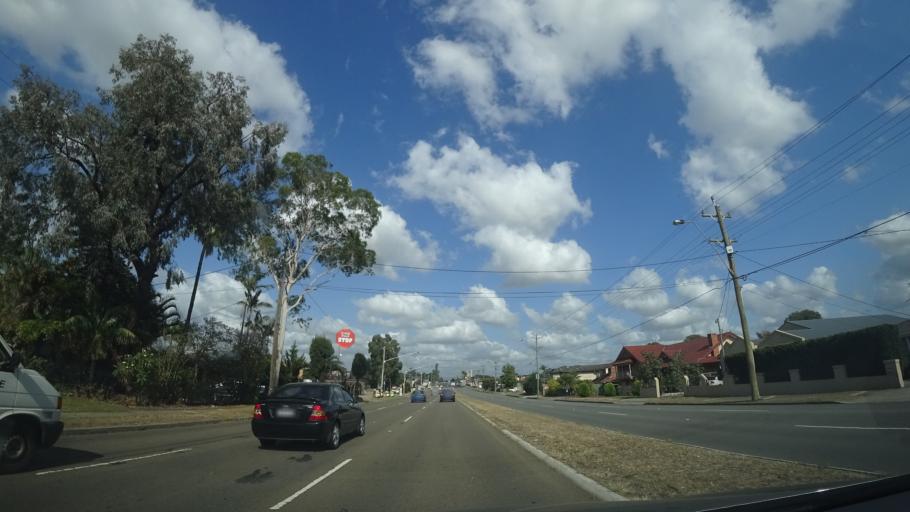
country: AU
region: New South Wales
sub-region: Fairfield
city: Chipping Norton
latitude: -33.9288
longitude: 150.9517
